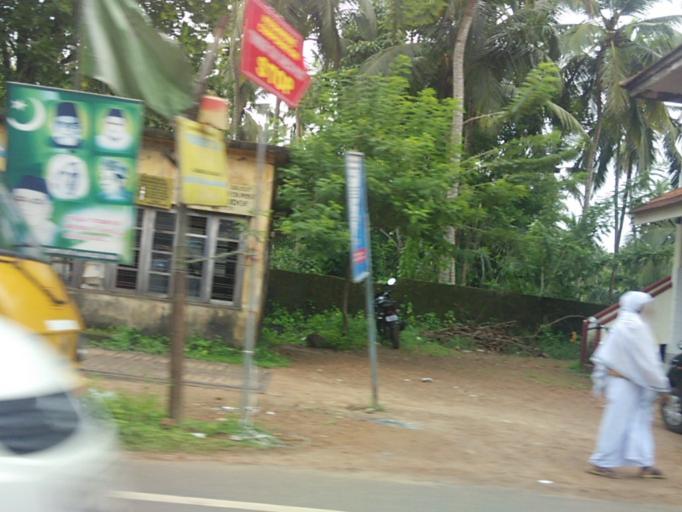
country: IN
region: Kerala
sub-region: Kozhikode
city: Kunnamangalam
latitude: 11.2977
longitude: 75.8509
